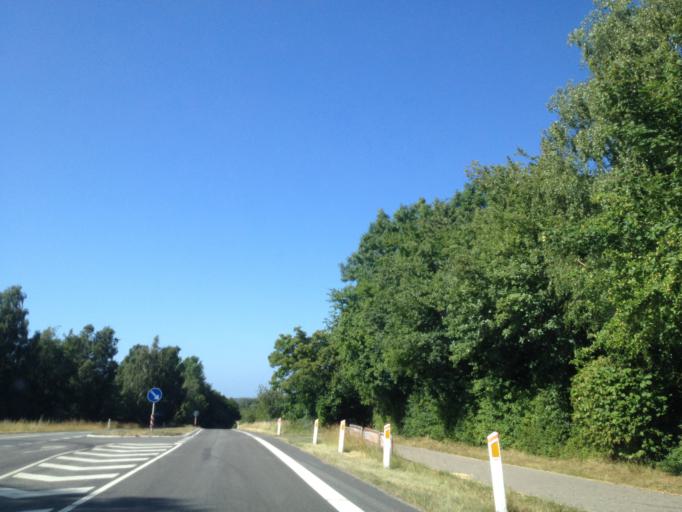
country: DK
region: Capital Region
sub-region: Gribskov Kommune
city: Graested
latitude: 56.0520
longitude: 12.3410
